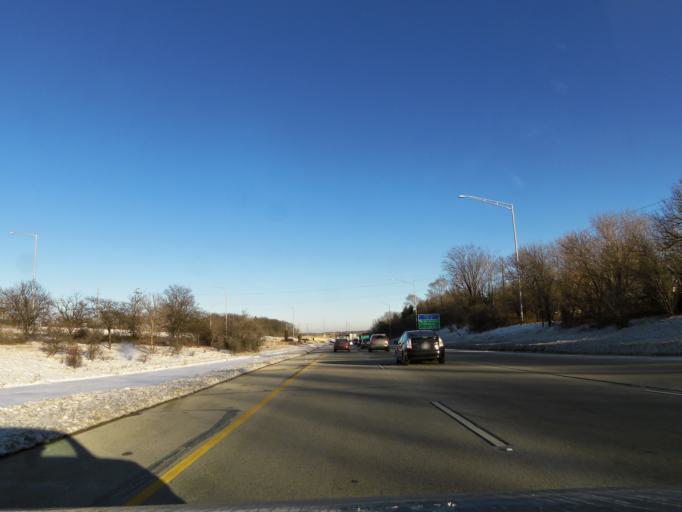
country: US
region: Wisconsin
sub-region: Milwaukee County
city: Greendale
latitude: 42.9610
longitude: -87.9635
